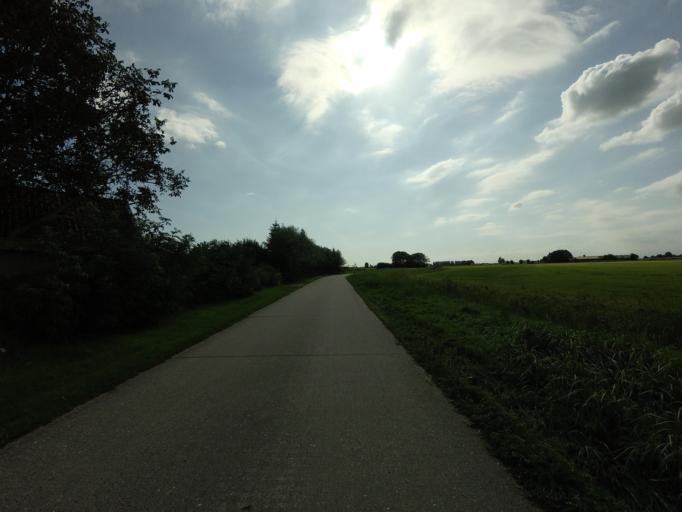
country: NL
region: Friesland
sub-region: Sudwest Fryslan
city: Scharnegoutum
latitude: 53.0785
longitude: 5.6323
